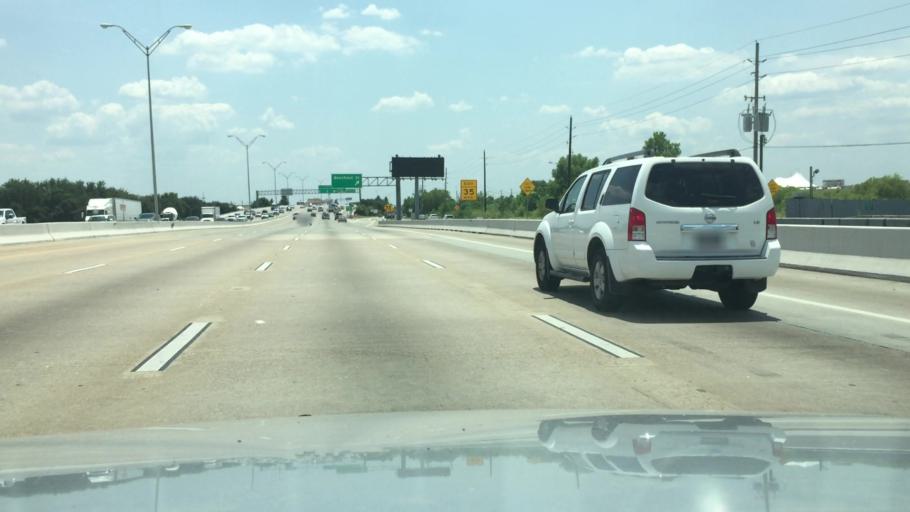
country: US
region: Texas
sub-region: Fort Bend County
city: Meadows Place
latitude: 29.6955
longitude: -95.5572
